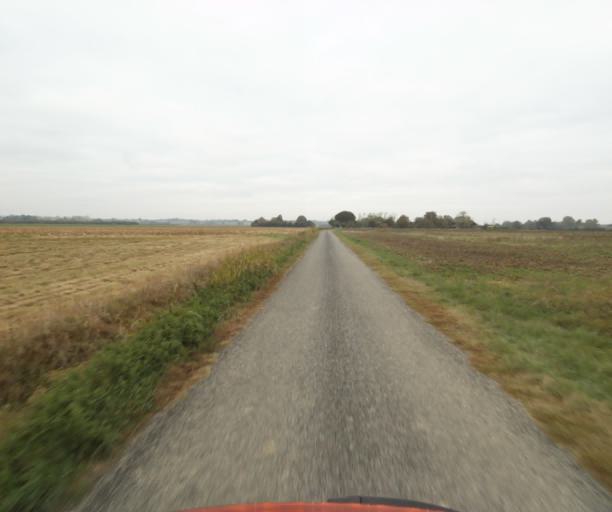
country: FR
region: Midi-Pyrenees
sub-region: Departement du Tarn-et-Garonne
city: Verdun-sur-Garonne
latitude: 43.8115
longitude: 1.2353
